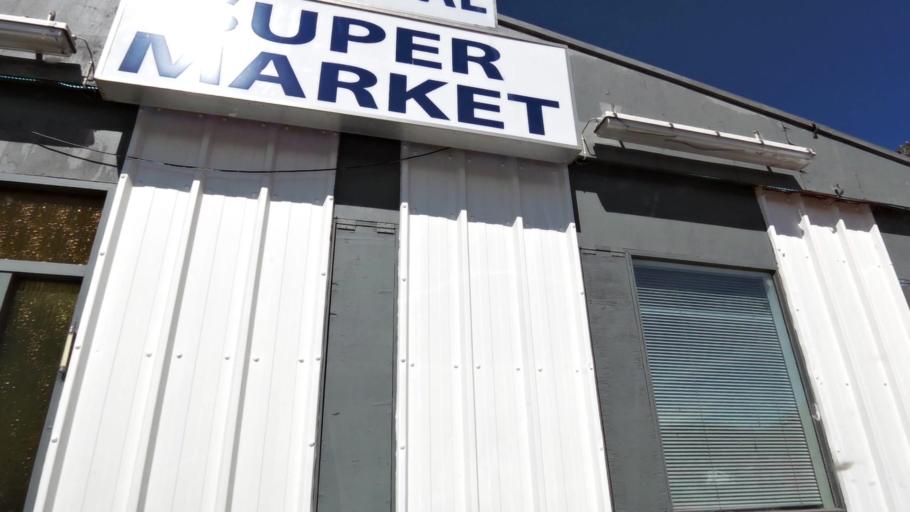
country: IS
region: West
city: Olafsvik
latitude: 65.5985
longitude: -24.0008
